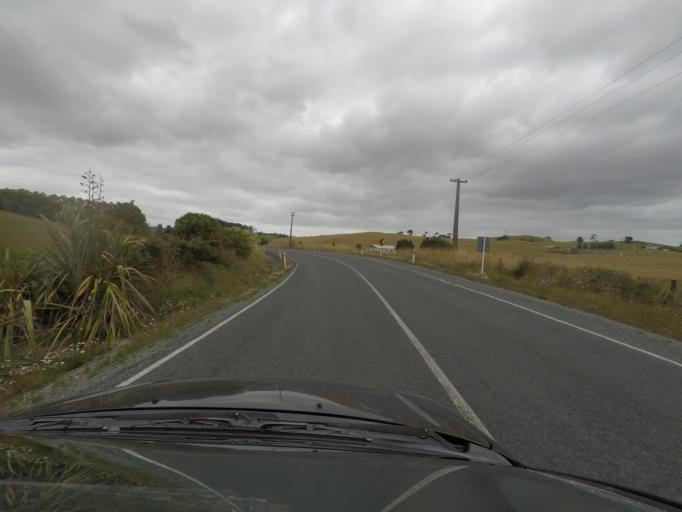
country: NZ
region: Auckland
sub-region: Auckland
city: Wellsford
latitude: -36.2827
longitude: 174.5552
